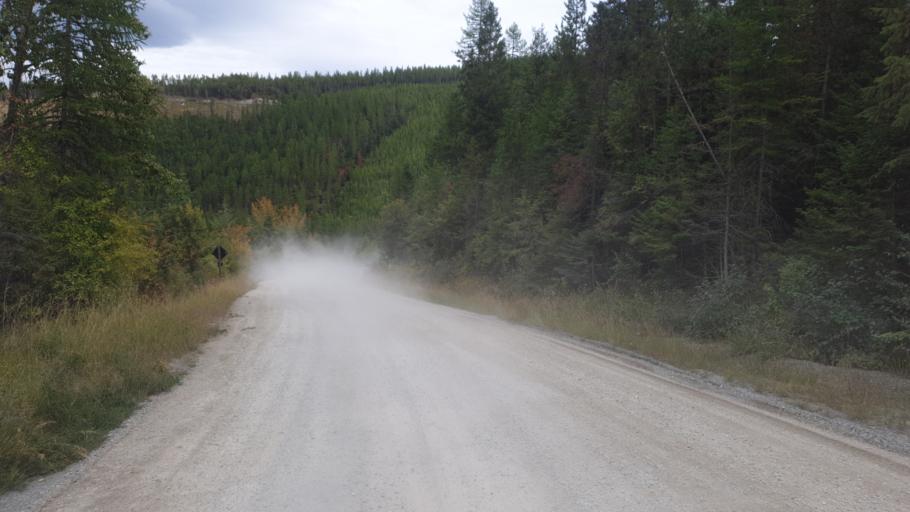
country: US
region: Montana
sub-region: Flathead County
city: Lakeside
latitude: 47.9898
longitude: -114.3182
